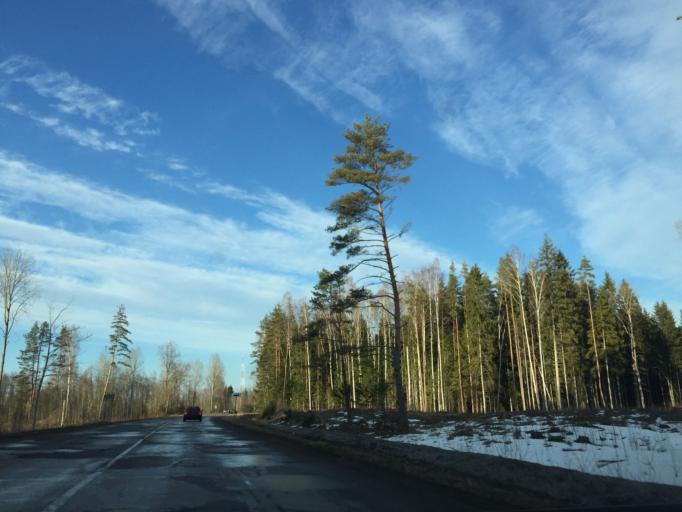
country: LV
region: Kekava
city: Balozi
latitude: 56.7623
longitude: 24.1076
